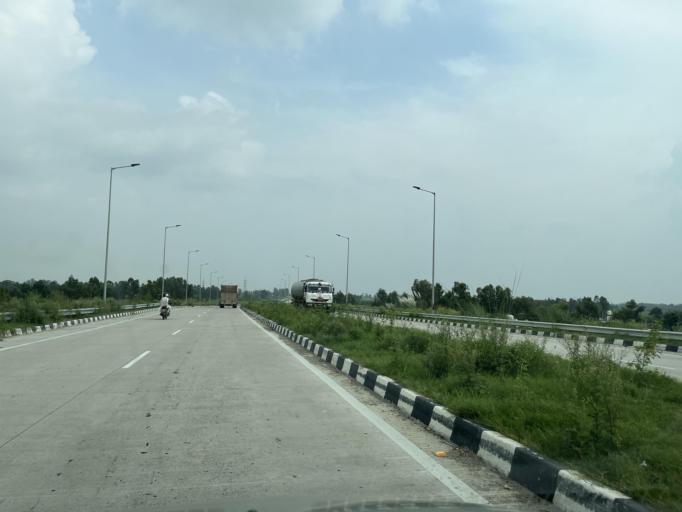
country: IN
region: Uttarakhand
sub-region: Udham Singh Nagar
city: Kashipur
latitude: 29.1725
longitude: 78.9489
